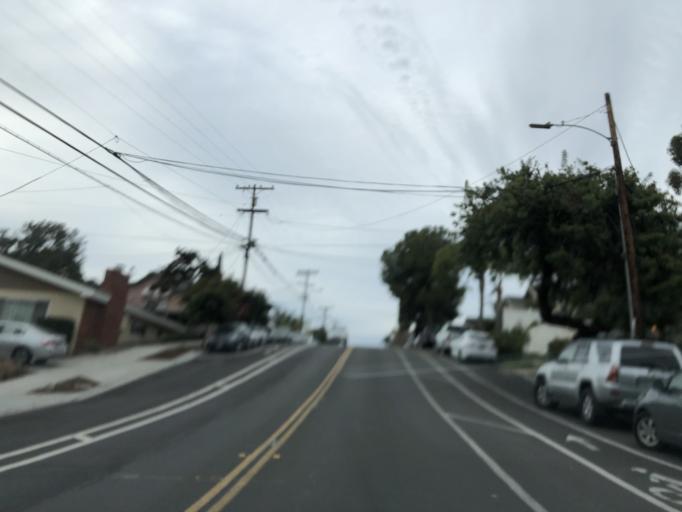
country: US
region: California
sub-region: San Diego County
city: San Diego
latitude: 32.7444
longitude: -117.1513
